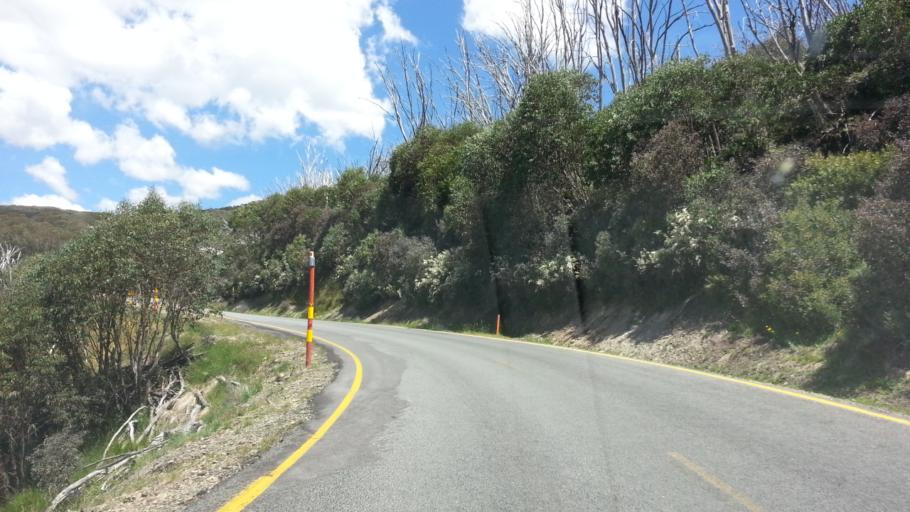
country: AU
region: Victoria
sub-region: Alpine
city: Mount Beauty
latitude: -36.8593
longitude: 147.2756
